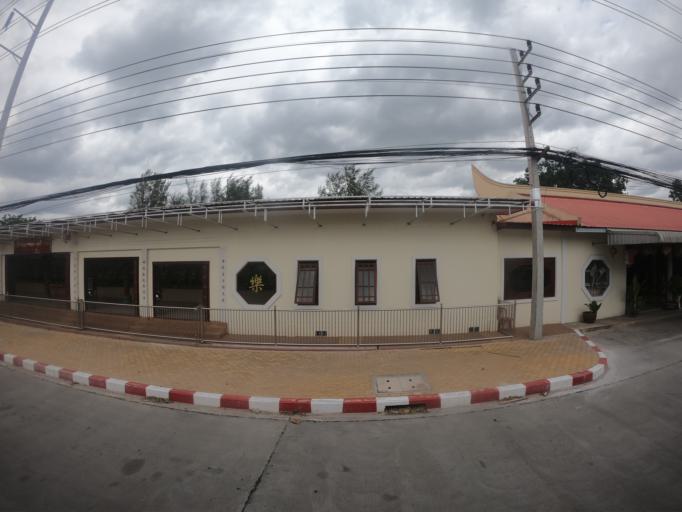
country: TH
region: Nakhon Ratchasima
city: Nakhon Ratchasima
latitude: 14.9508
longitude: 102.1243
